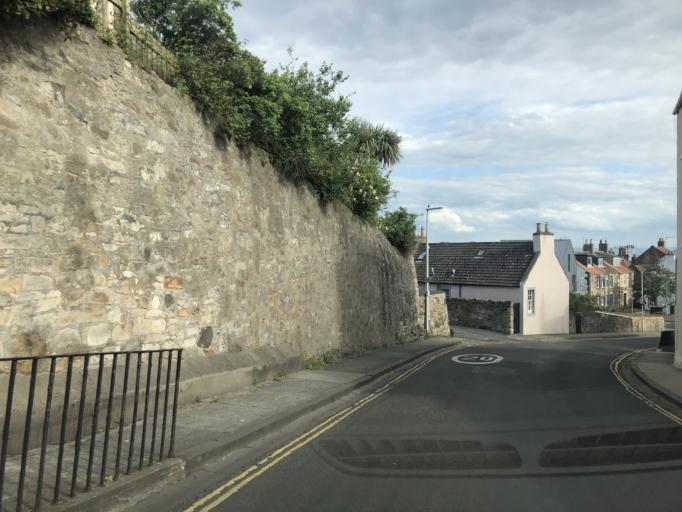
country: GB
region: Scotland
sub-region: Fife
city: Saint Monance
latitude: 56.2062
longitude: -2.7655
